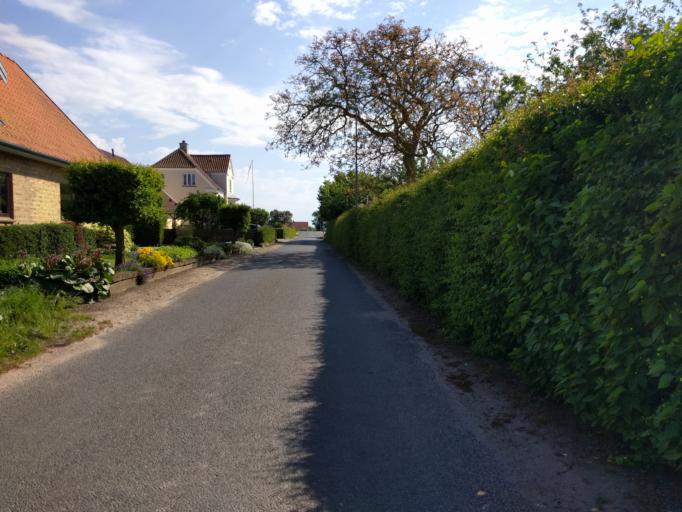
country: DK
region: South Denmark
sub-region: Kerteminde Kommune
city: Munkebo
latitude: 55.4809
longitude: 10.5970
